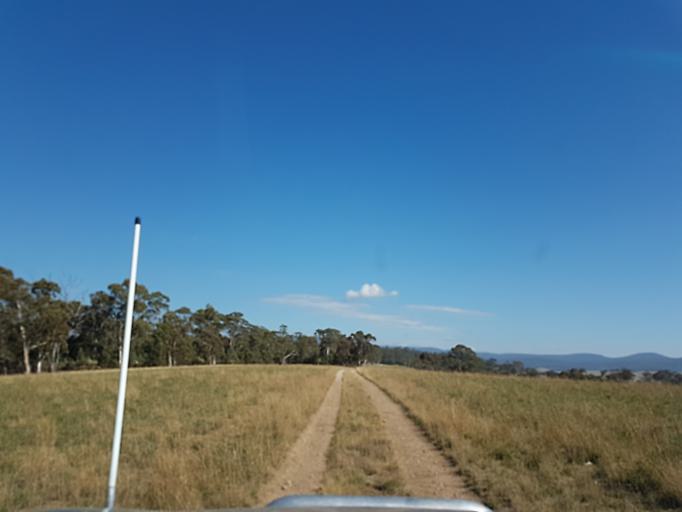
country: AU
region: New South Wales
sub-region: Snowy River
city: Jindabyne
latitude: -37.0454
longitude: 148.2867
